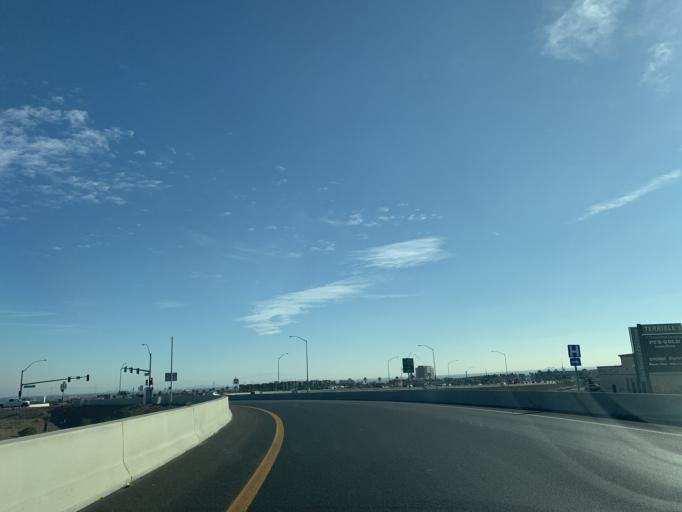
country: US
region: Nevada
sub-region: Clark County
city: Summerlin South
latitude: 36.2979
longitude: -115.2880
